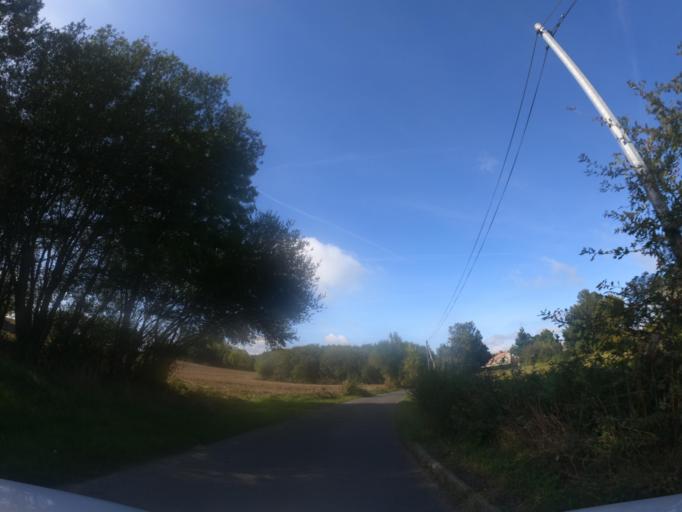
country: FR
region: Poitou-Charentes
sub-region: Departement des Deux-Sevres
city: Courlay
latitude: 46.7908
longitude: -0.5838
